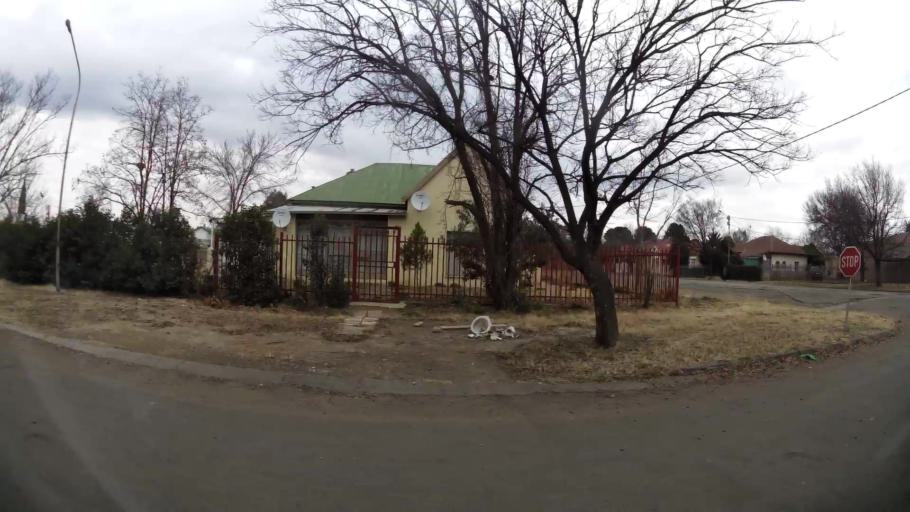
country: ZA
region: Orange Free State
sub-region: Fezile Dabi District Municipality
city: Kroonstad
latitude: -27.6586
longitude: 27.2420
